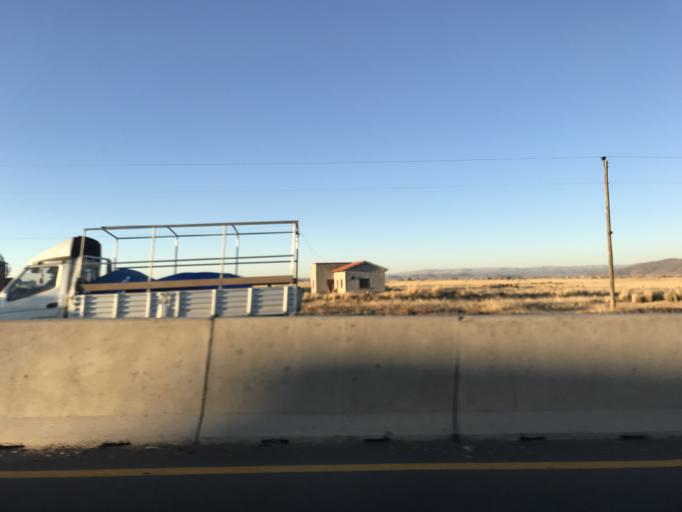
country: BO
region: La Paz
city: Batallas
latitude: -16.2989
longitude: -68.5025
